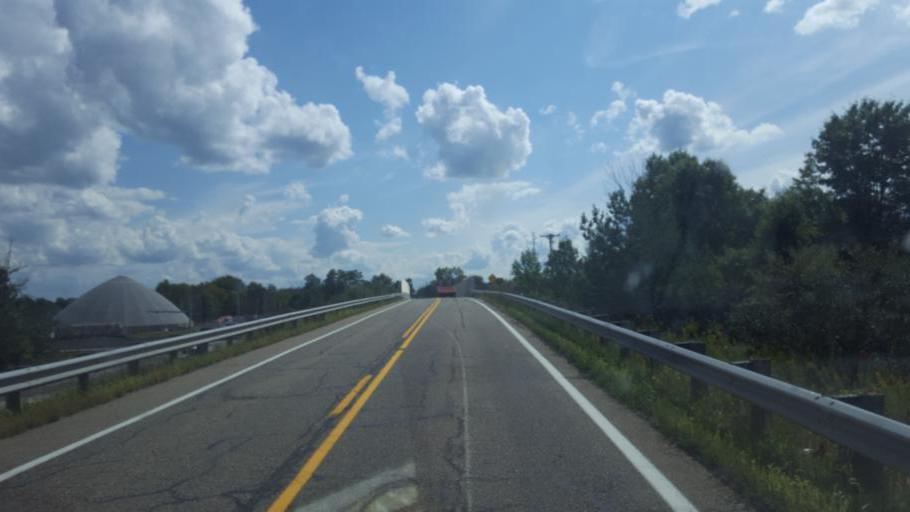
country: US
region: Ohio
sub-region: Portage County
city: Garrettsville
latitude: 41.2442
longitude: -81.1484
